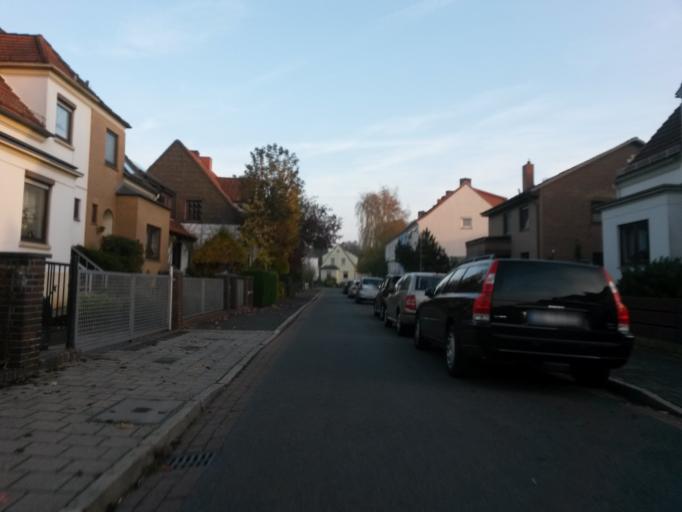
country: DE
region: Bremen
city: Bremen
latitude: 53.0499
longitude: 8.8236
